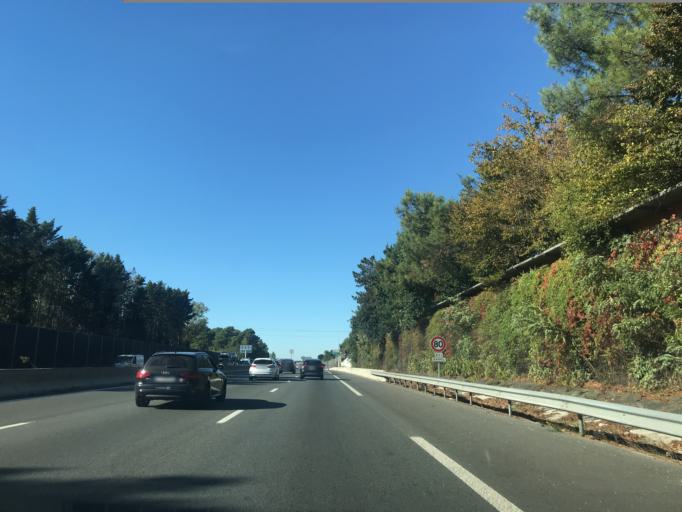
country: FR
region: Aquitaine
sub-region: Departement de la Gironde
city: Pessac
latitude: 44.7950
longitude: -0.6506
